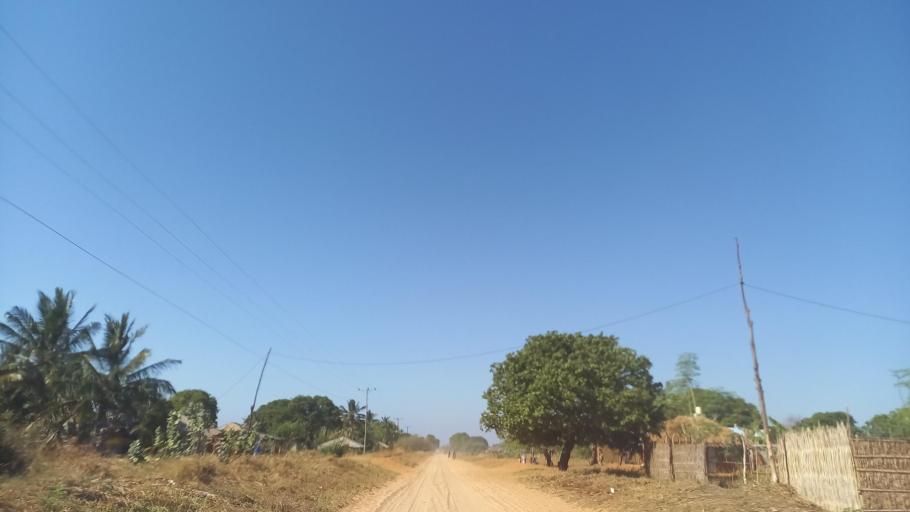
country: MZ
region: Cabo Delgado
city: Pemba
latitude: -13.1486
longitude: 40.5569
